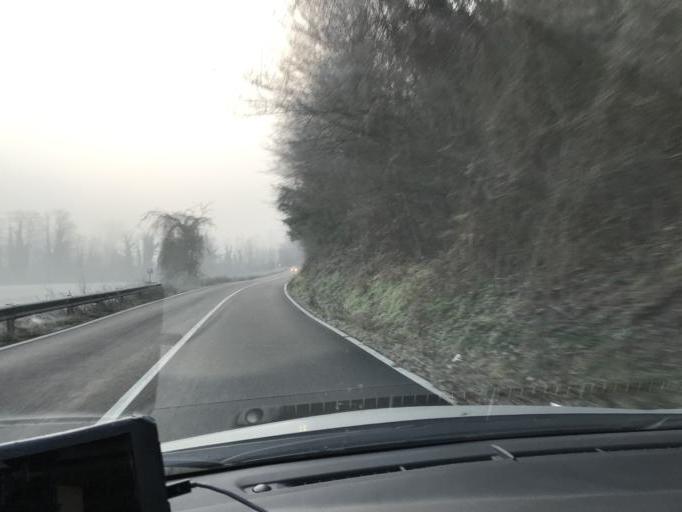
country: IT
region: Latium
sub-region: Provincia di Rieti
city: Colli sul Velino
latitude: 42.5181
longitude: 12.7367
